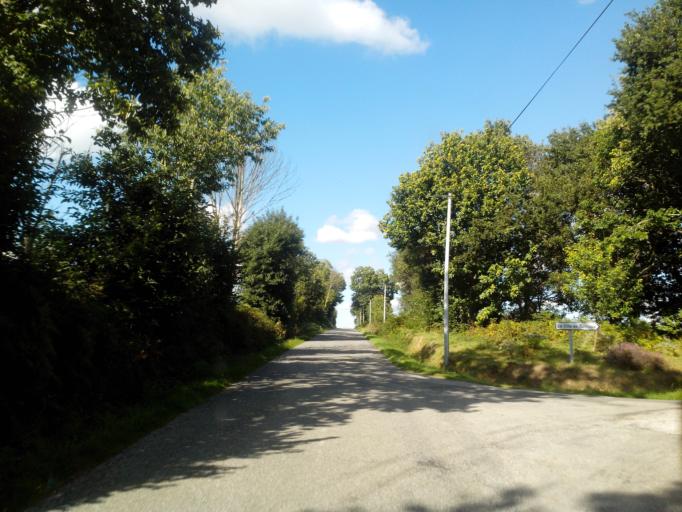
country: FR
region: Brittany
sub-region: Departement des Cotes-d'Armor
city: Merdrignac
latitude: 48.1617
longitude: -2.4190
